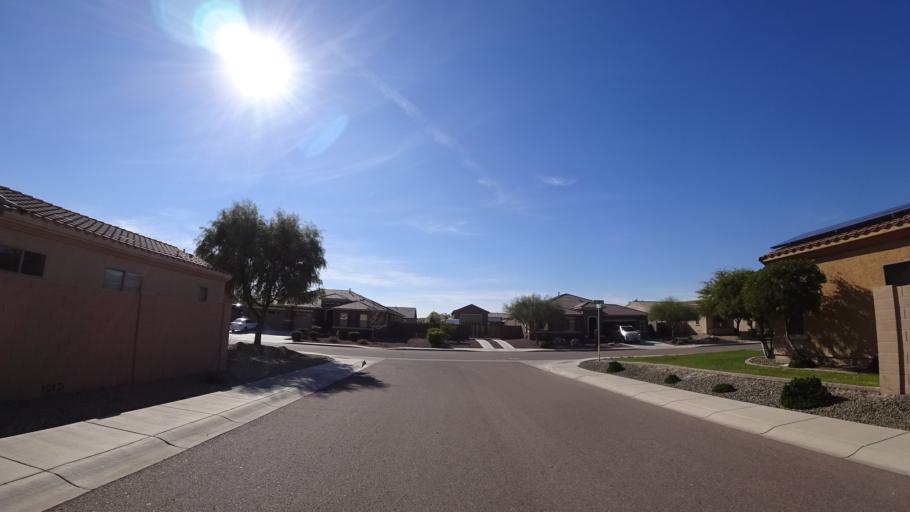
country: US
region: Arizona
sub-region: Maricopa County
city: Citrus Park
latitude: 33.5161
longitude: -112.4569
